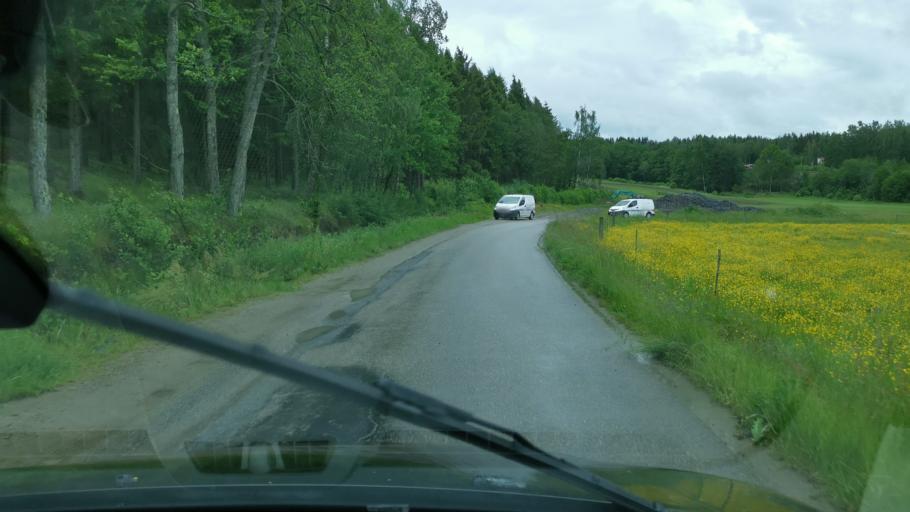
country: SE
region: Vaestra Goetaland
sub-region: Orust
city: Henan
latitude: 58.3218
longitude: 11.7177
